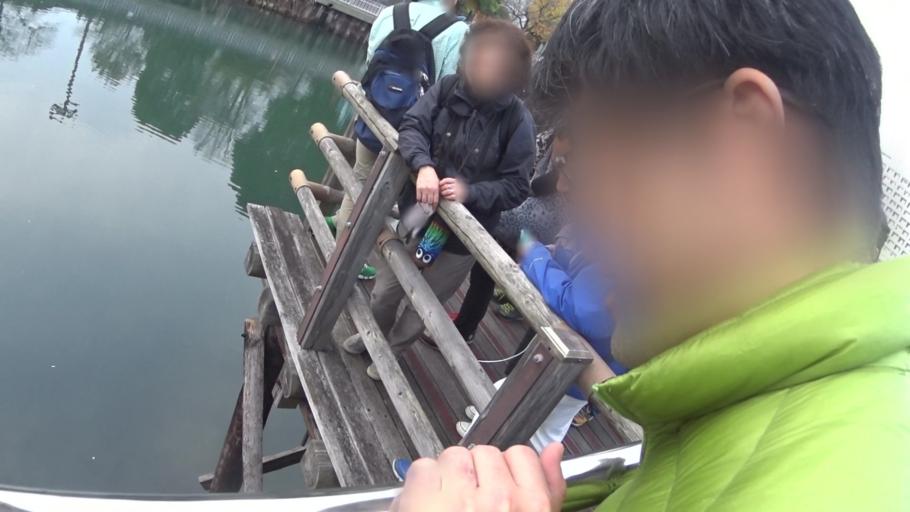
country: JP
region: Tokyo
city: Urayasu
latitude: 35.6918
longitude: 139.8205
